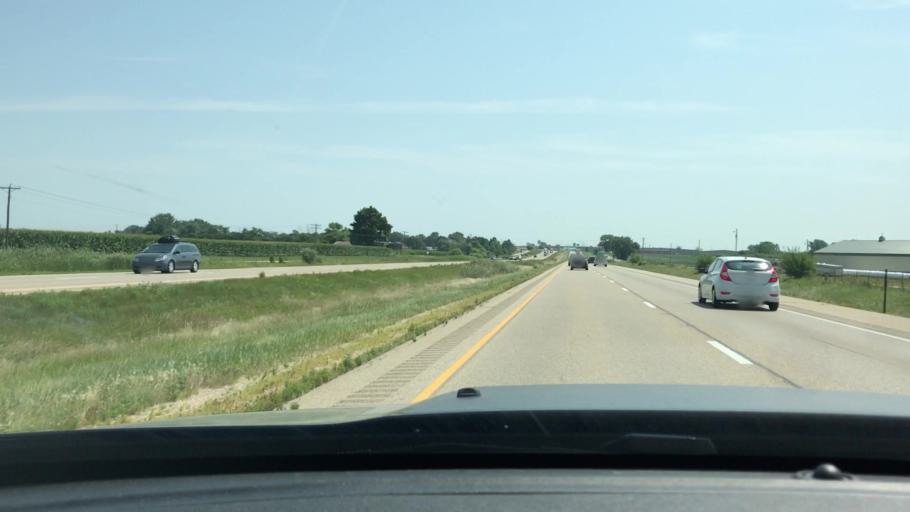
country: US
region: Illinois
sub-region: Bureau County
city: Spring Valley
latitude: 41.3644
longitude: -89.1705
